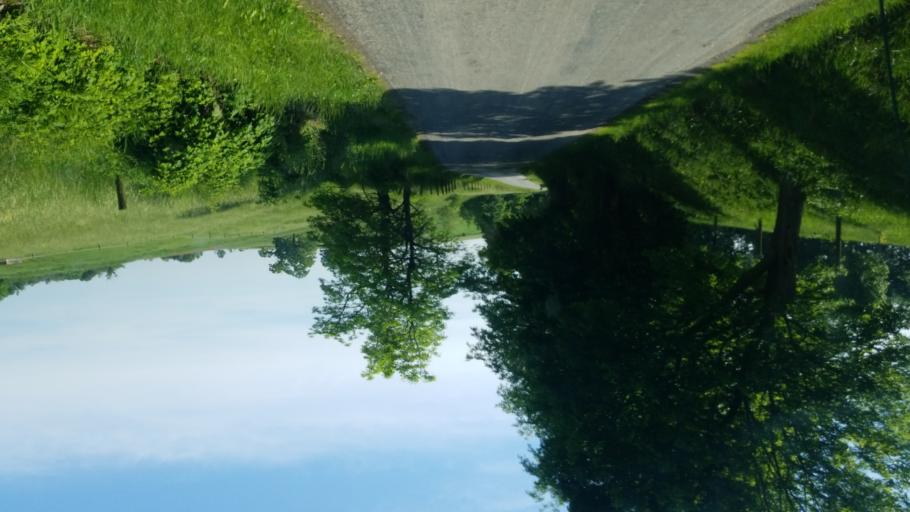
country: US
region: Ohio
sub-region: Tuscarawas County
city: Sugarcreek
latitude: 40.4872
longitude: -81.7699
